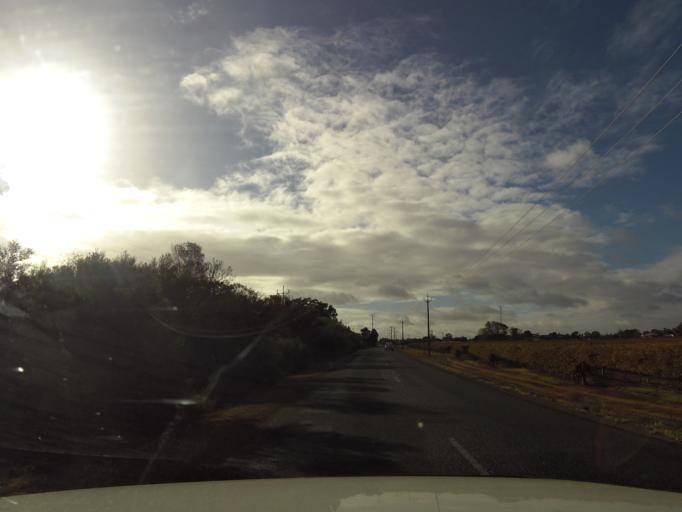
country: AU
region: South Australia
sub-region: Berri and Barmera
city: Berri
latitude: -34.2714
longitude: 140.5846
